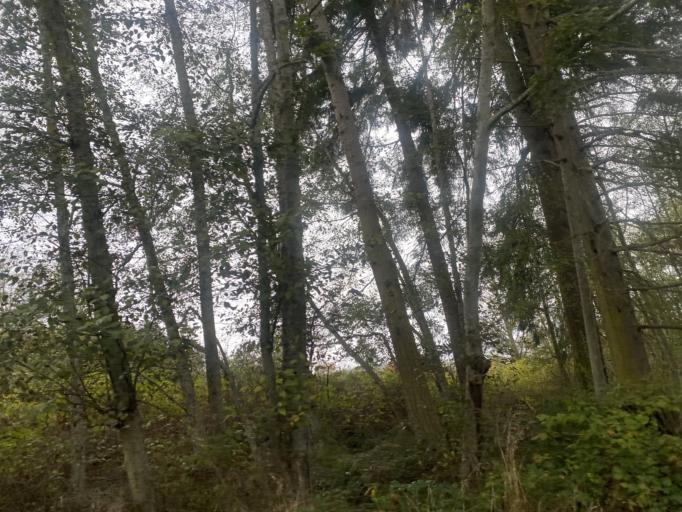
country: US
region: Washington
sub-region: Island County
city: Freeland
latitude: 48.0896
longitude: -122.5668
